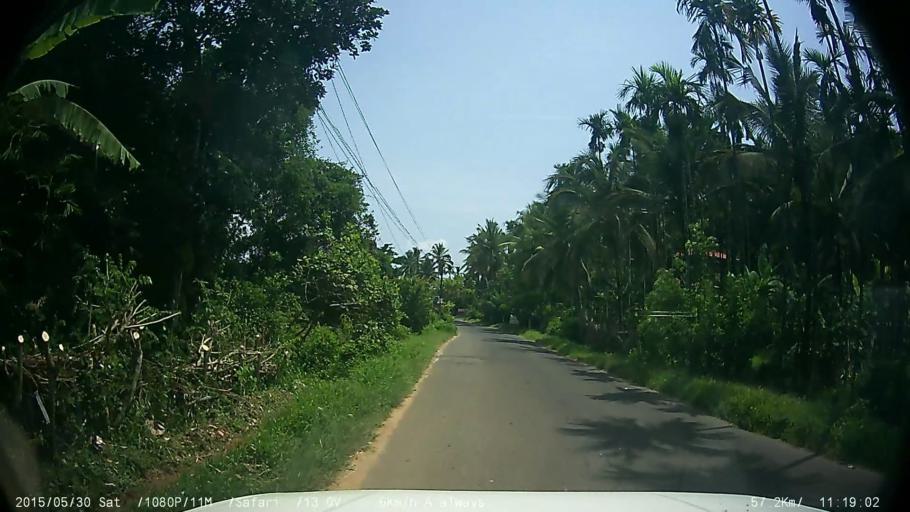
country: IN
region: Kerala
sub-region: Wayanad
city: Panamaram
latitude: 11.7873
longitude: 76.0455
